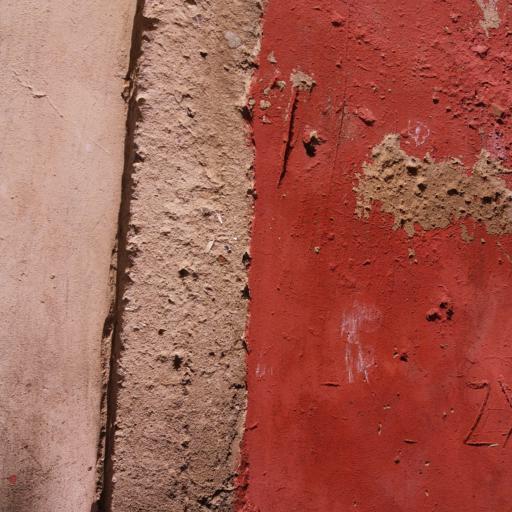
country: MZ
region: Maputo City
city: Maputo
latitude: -25.9038
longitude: 32.5915
